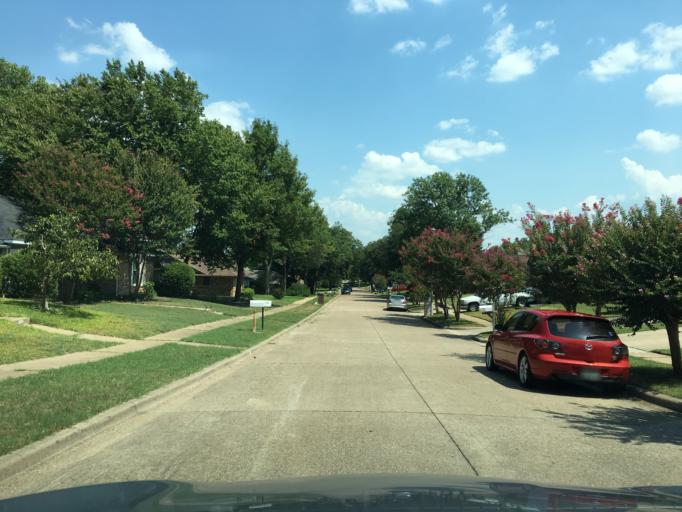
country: US
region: Texas
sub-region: Collin County
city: Plano
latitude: 32.9682
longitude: -96.6700
